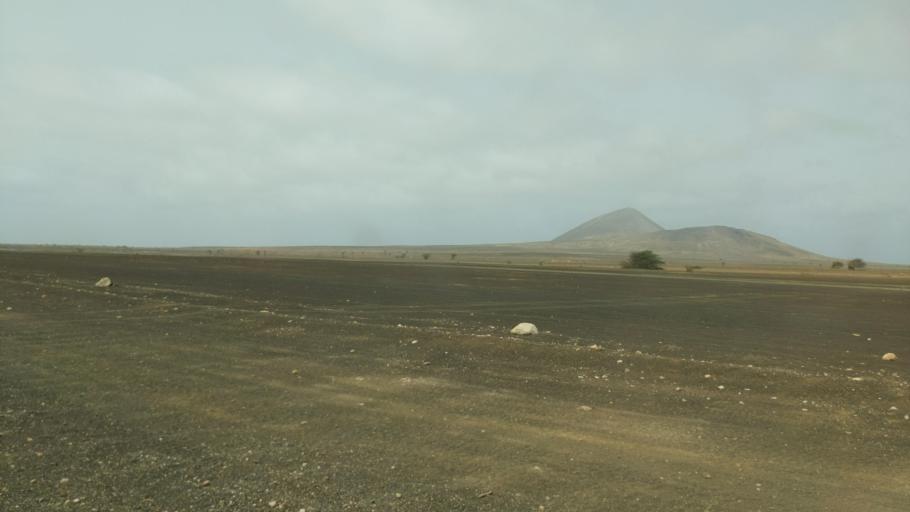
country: CV
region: Sal
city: Espargos
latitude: 16.7950
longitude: -22.9518
